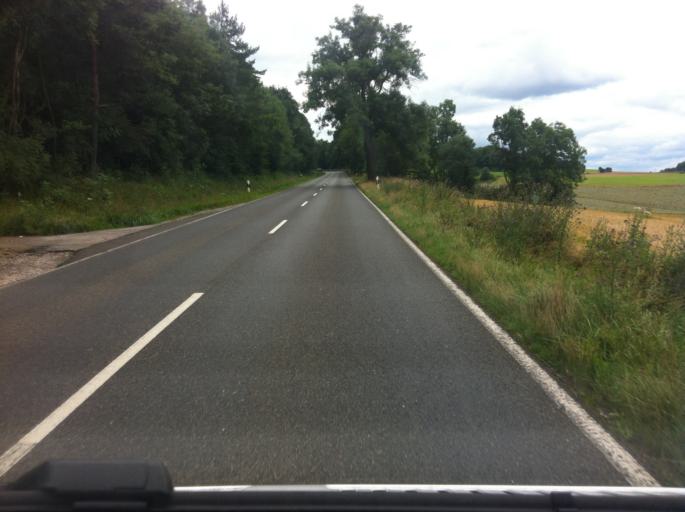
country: DE
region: North Rhine-Westphalia
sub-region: Regierungsbezirk Koln
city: Nettersheim
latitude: 50.5227
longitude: 6.6565
